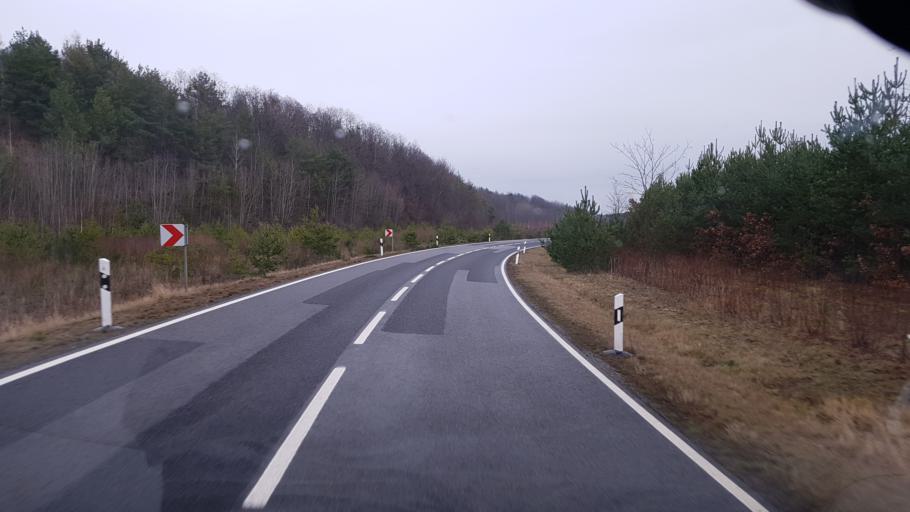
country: DE
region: Brandenburg
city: Schipkau
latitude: 51.5060
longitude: 13.8671
